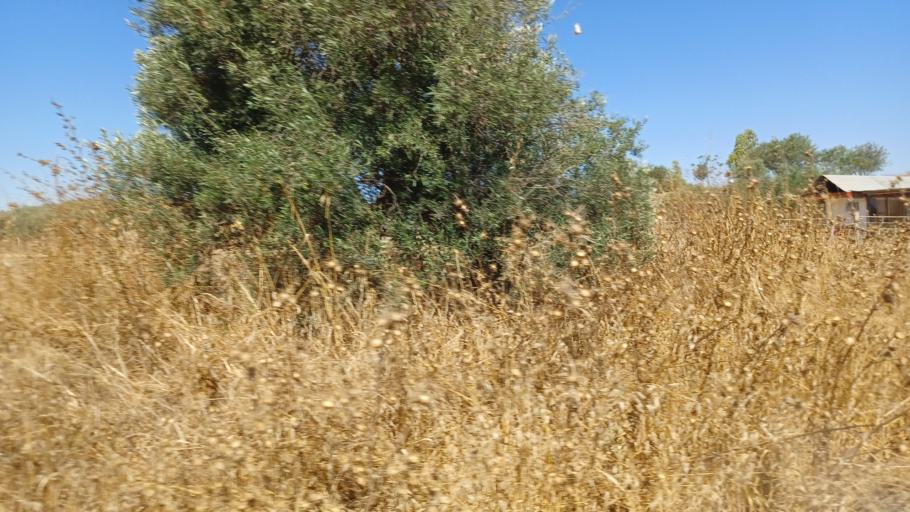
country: CY
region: Ammochostos
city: Avgorou
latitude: 35.0528
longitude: 33.8321
